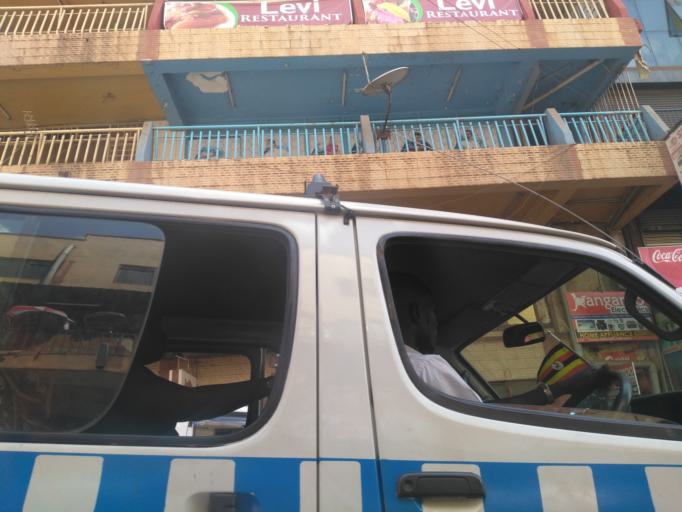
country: UG
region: Central Region
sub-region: Kampala District
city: Kampala
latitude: 0.3117
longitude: 32.5781
